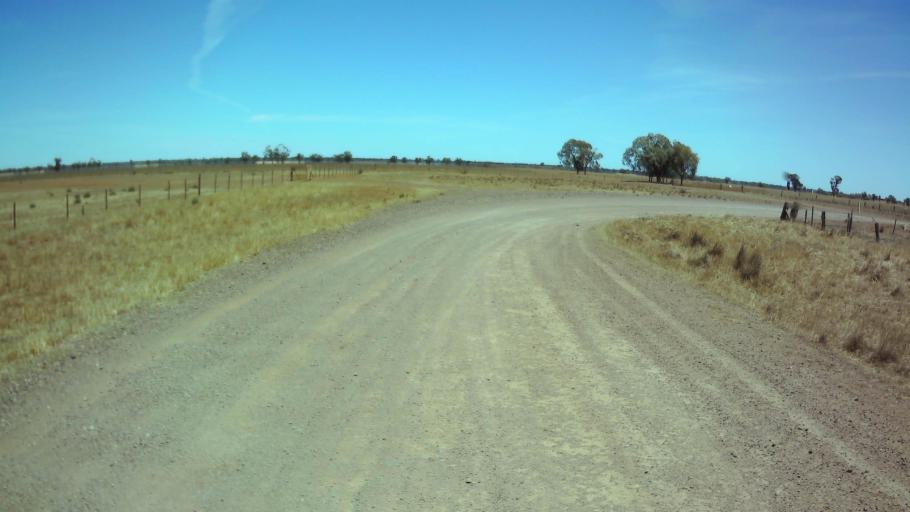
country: AU
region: New South Wales
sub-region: Forbes
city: Forbes
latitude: -33.6956
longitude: 147.6714
